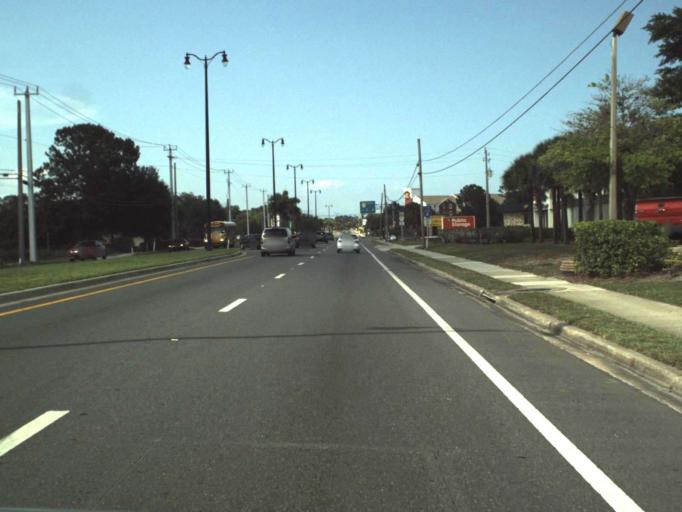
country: US
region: Florida
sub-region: Seminole County
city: Sanford
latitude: 28.7740
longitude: -81.2781
